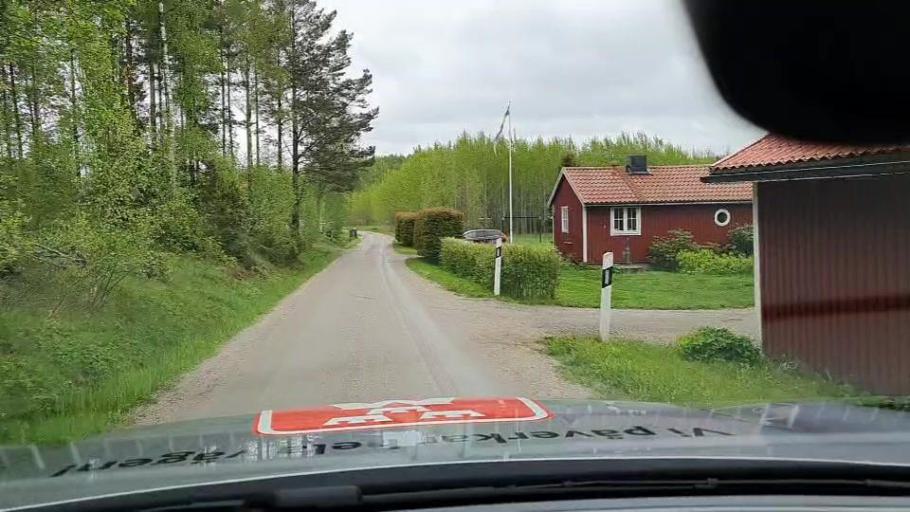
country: SE
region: Soedermanland
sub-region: Nykopings Kommun
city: Svalsta
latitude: 58.6237
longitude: 16.9385
